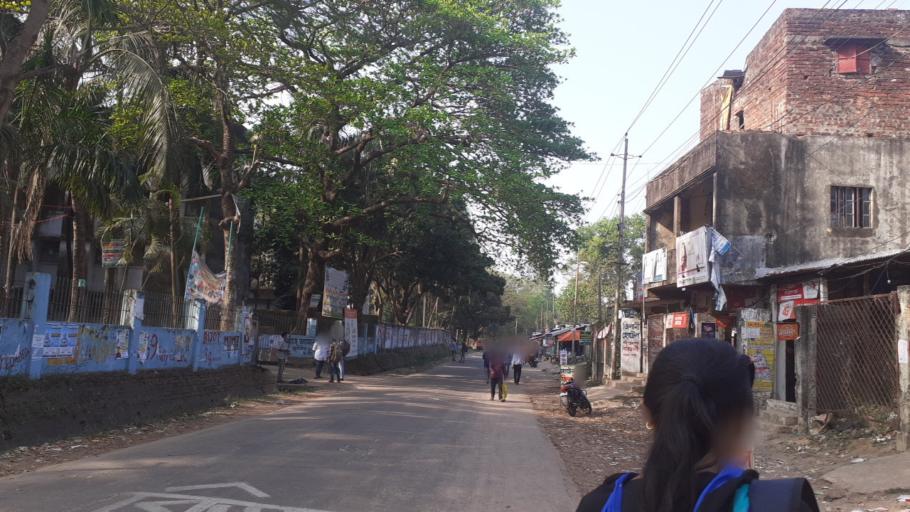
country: BD
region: Chittagong
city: Chittagong
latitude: 22.4727
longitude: 91.7933
